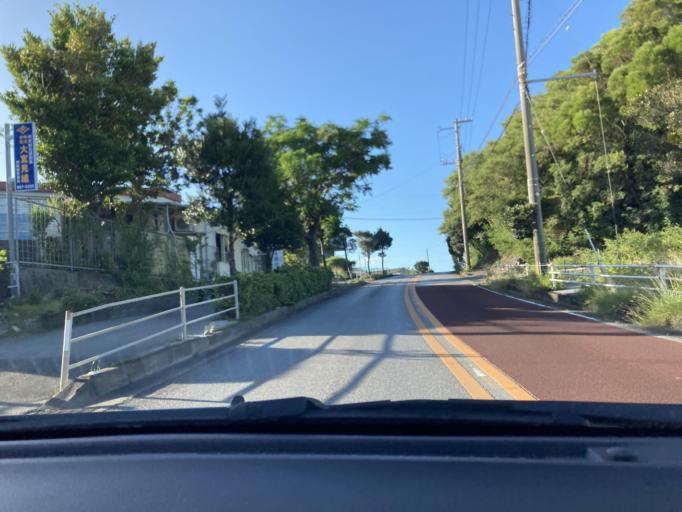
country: JP
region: Okinawa
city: Tomigusuku
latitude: 26.1853
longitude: 127.7307
